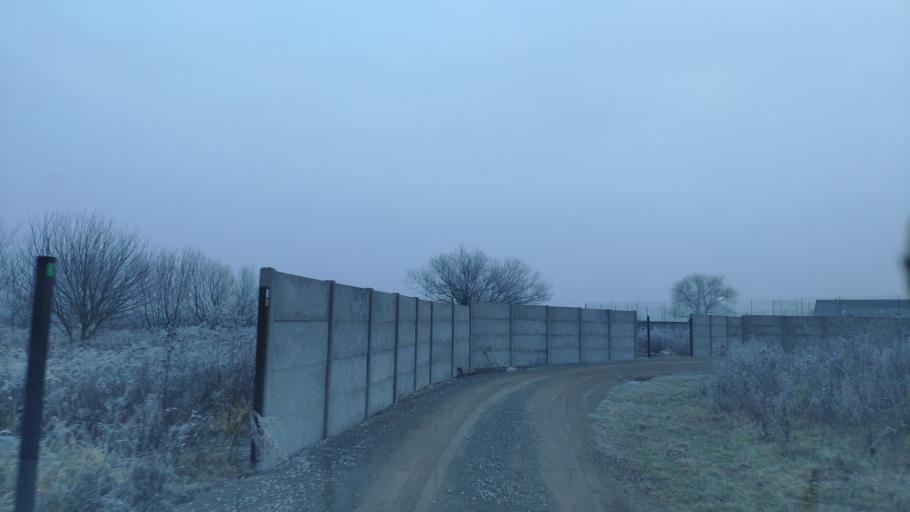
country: SK
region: Kosicky
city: Kosice
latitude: 48.6183
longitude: 21.3265
